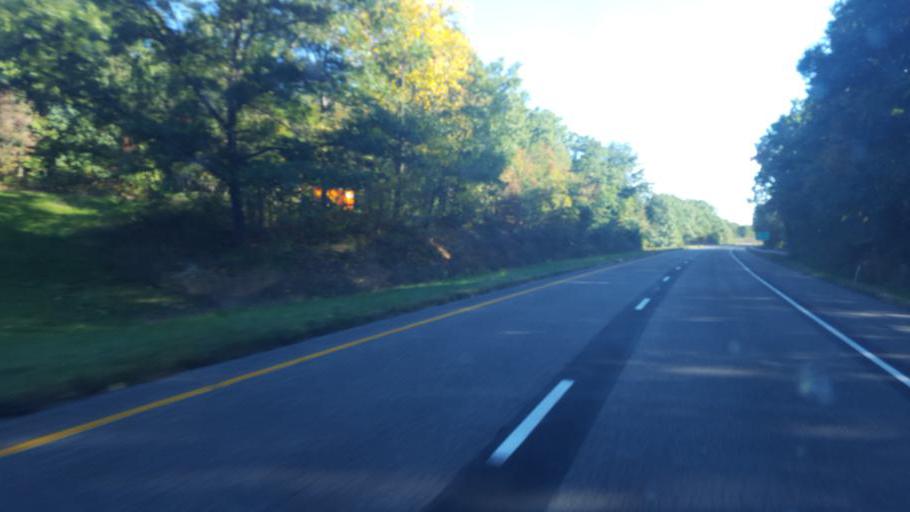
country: US
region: West Virginia
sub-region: Morgan County
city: Berkeley Springs
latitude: 39.6947
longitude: -78.3940
